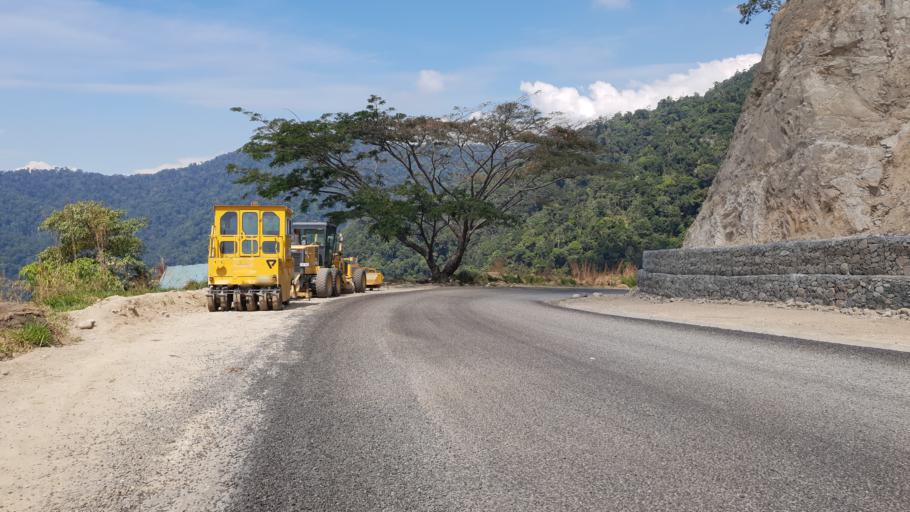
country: PG
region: Eastern Highlands
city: Kainantu
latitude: -6.1982
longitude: 146.0419
